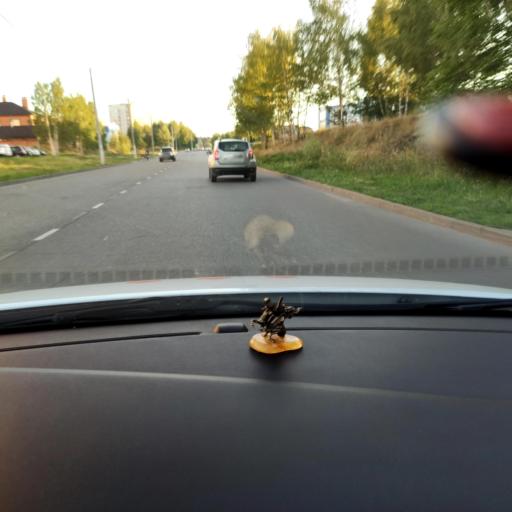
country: RU
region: Tatarstan
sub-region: Zelenodol'skiy Rayon
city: Zelenodolsk
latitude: 55.8668
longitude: 48.5644
